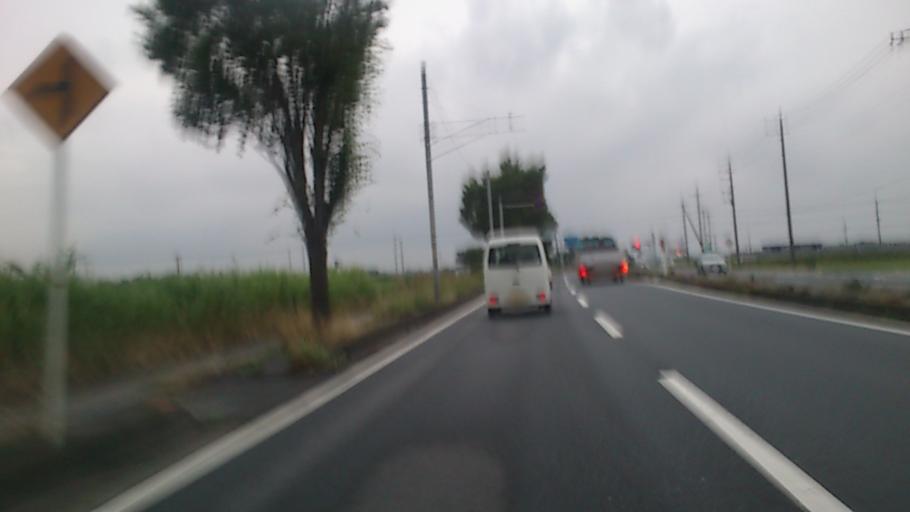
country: JP
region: Saitama
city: Hanyu
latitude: 36.1520
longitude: 139.5106
